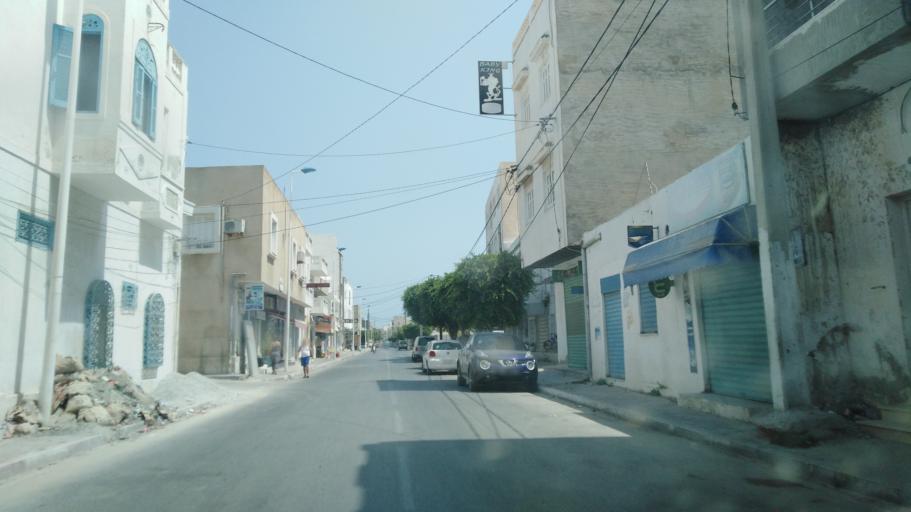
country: TN
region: Al Mahdiyah
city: Mahdia
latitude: 35.5119
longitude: 11.0475
